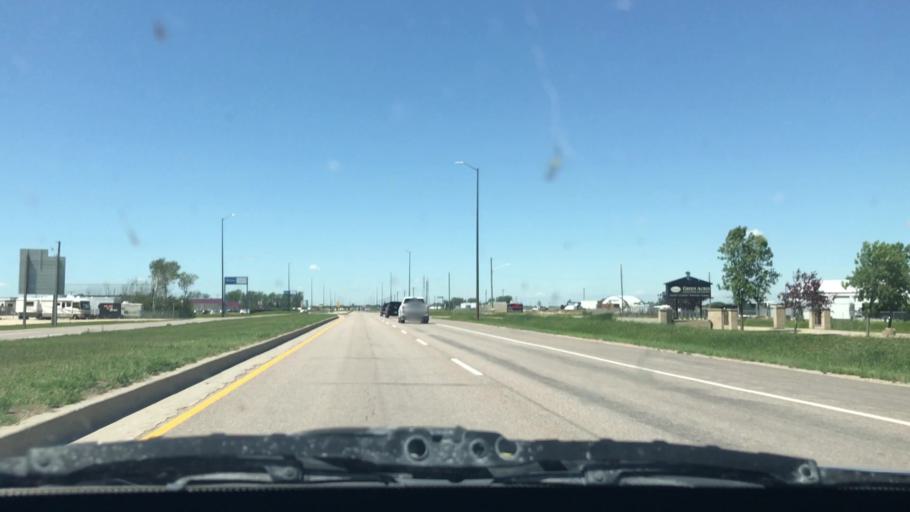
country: CA
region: Manitoba
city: Winnipeg
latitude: 49.8445
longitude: -96.9922
